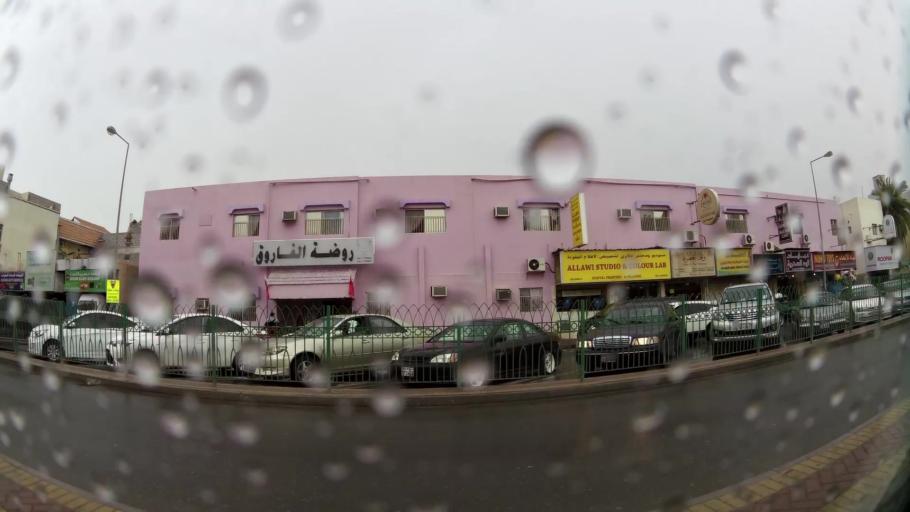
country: BH
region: Northern
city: Madinat `Isa
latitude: 26.1748
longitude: 50.5573
